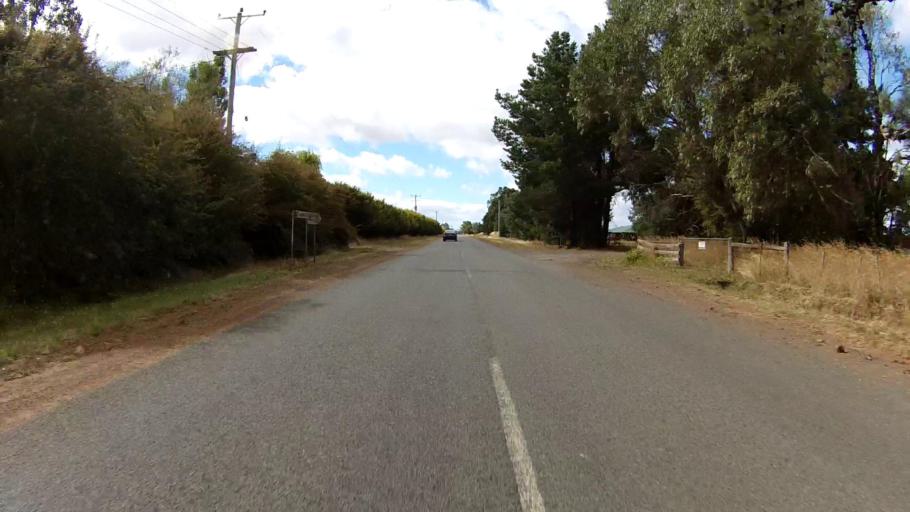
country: AU
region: Tasmania
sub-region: Northern Midlands
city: Evandale
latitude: -41.6070
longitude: 147.2835
